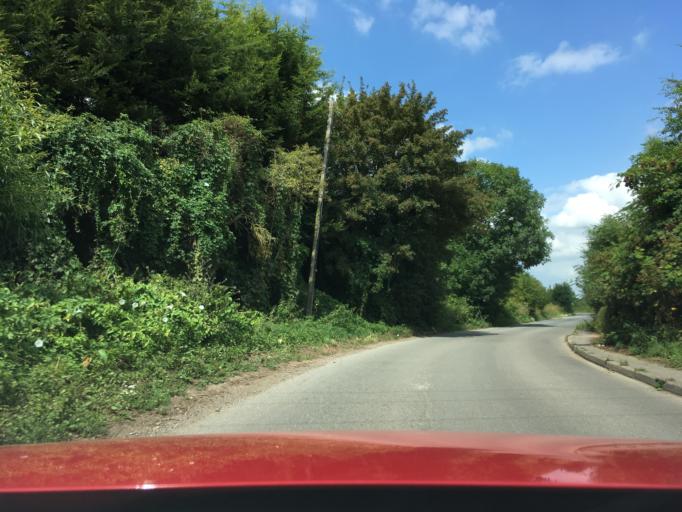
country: GB
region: England
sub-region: Gloucestershire
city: Gloucester
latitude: 51.8833
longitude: -2.2490
